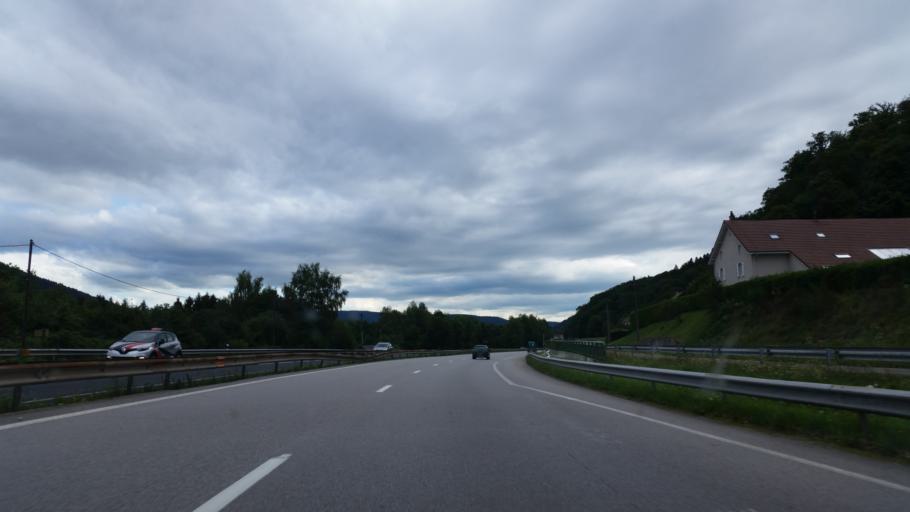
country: FR
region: Lorraine
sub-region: Departement des Vosges
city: Saint-Nabord
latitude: 48.0666
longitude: 6.5973
